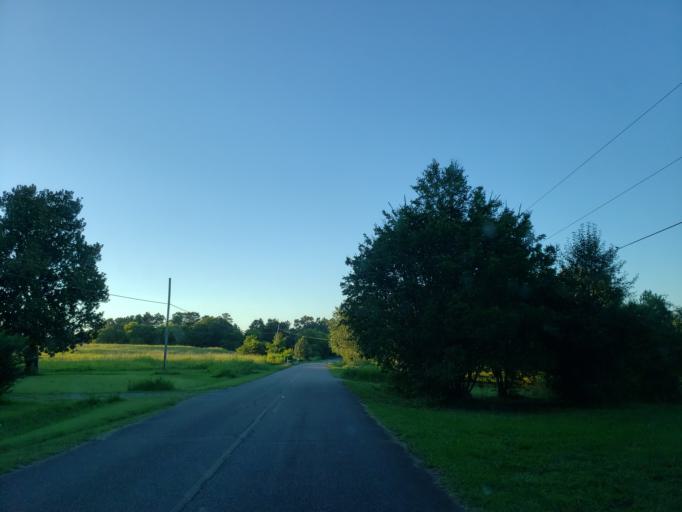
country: US
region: Georgia
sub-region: Bartow County
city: Euharlee
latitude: 34.0827
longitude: -84.9101
